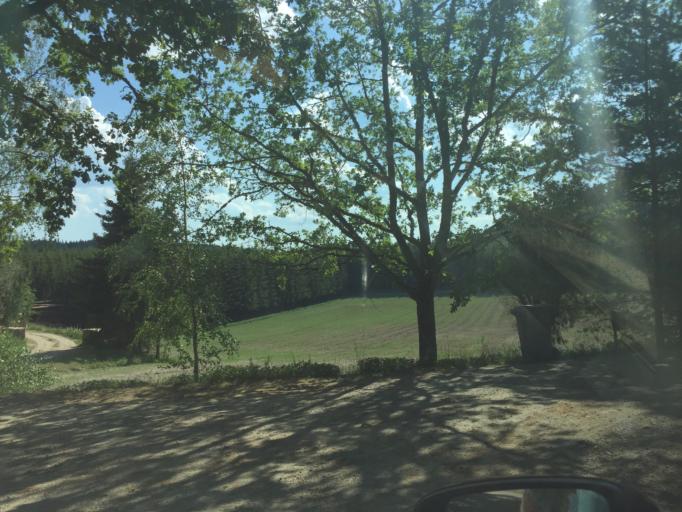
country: SE
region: Soedermanland
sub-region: Flens Kommun
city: Halleforsnas
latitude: 59.0639
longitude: 16.4107
